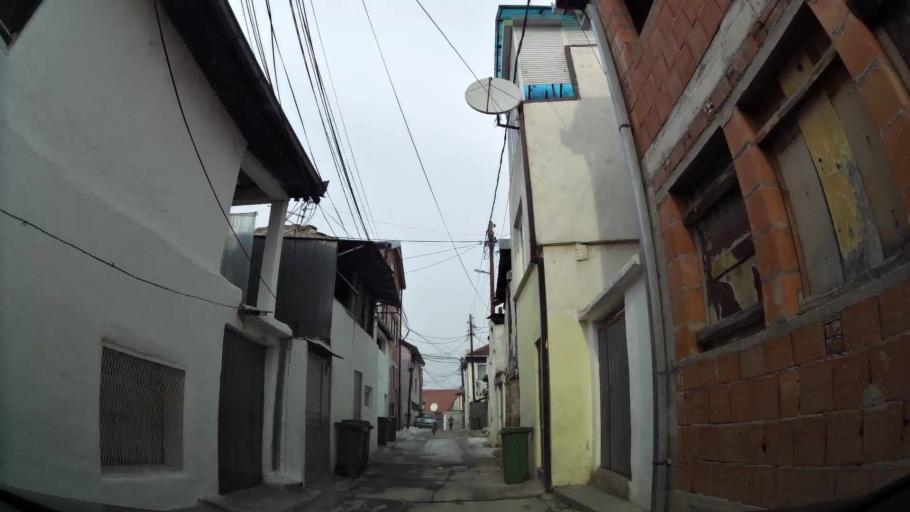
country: MK
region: Cair
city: Cair
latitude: 42.0039
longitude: 21.4485
